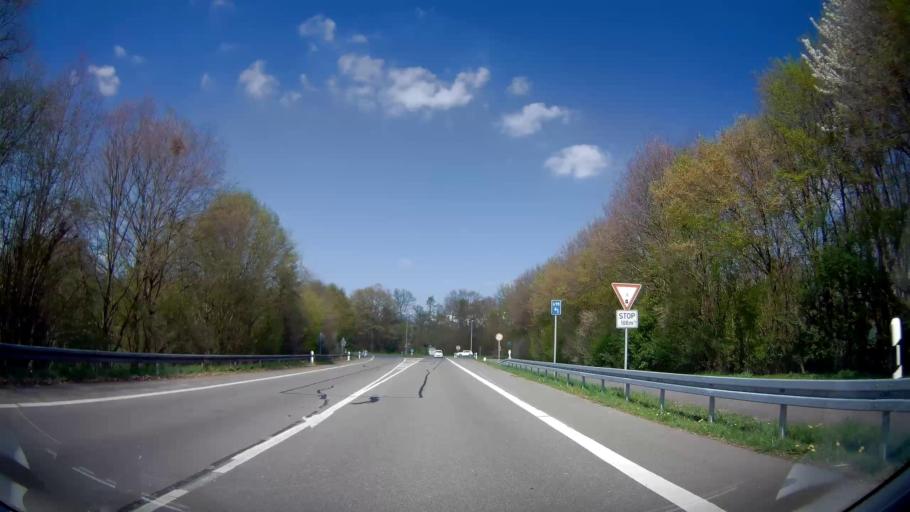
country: DE
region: North Rhine-Westphalia
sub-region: Regierungsbezirk Munster
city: Klein Reken
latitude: 51.7237
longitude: 7.0422
